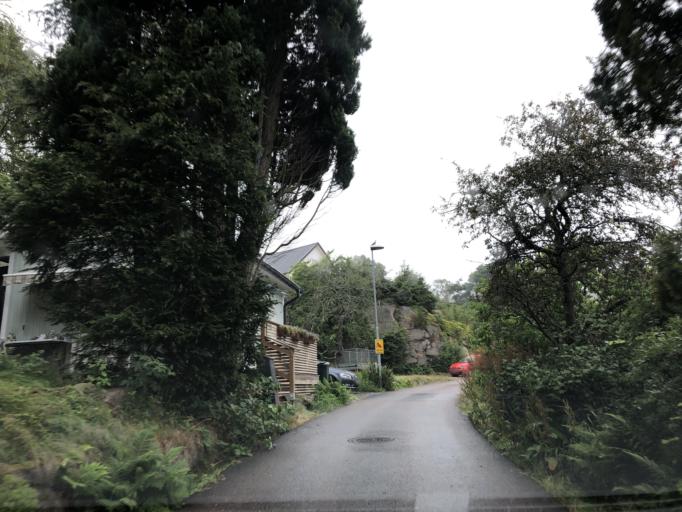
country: SE
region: Vaestra Goetaland
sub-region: Goteborg
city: Goeteborg
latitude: 57.7372
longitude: 11.9359
